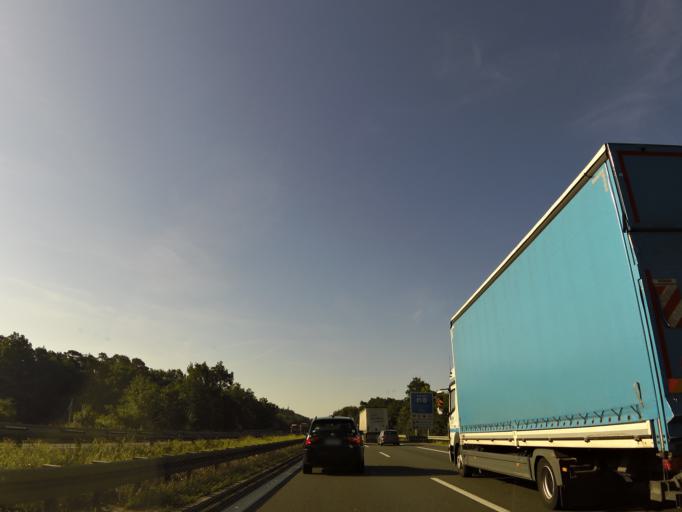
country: DE
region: Bavaria
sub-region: Regierungsbezirk Mittelfranken
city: Hessdorf
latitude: 49.6201
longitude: 10.9211
